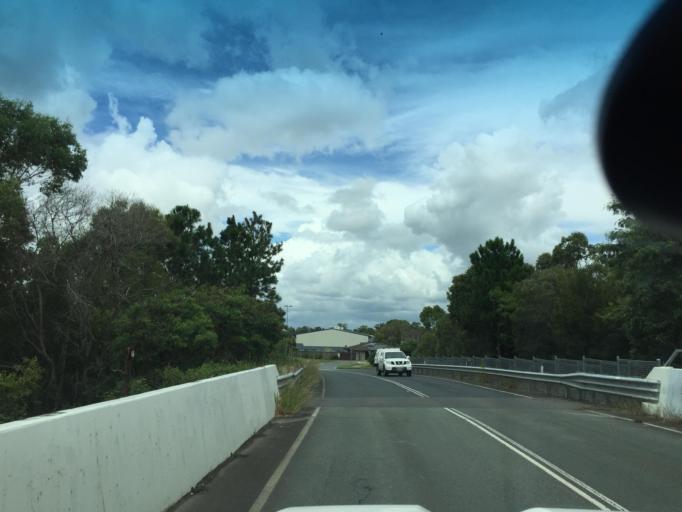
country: AU
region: Queensland
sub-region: Moreton Bay
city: Caboolture
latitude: -27.0675
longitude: 152.9329
